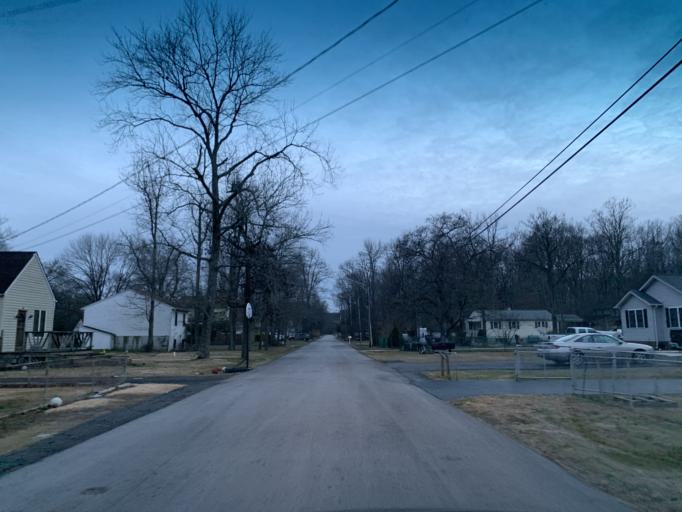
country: US
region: Maryland
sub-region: Baltimore County
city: Edgemere
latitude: 39.2813
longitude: -76.4187
